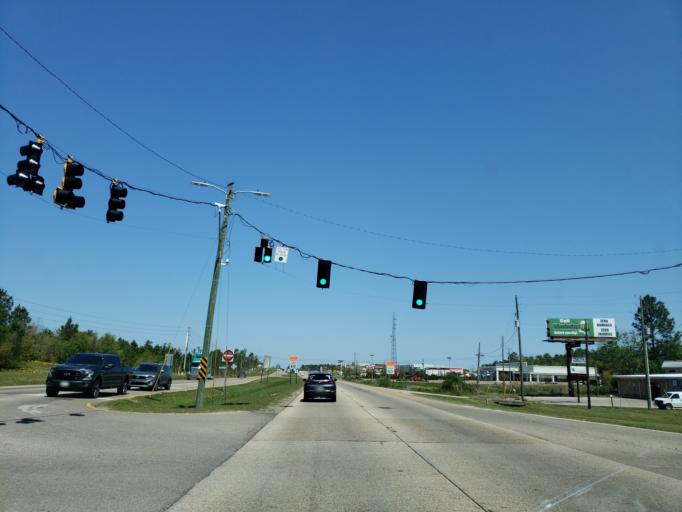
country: US
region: Mississippi
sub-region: Harrison County
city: Lyman
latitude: 30.4819
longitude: -89.1032
